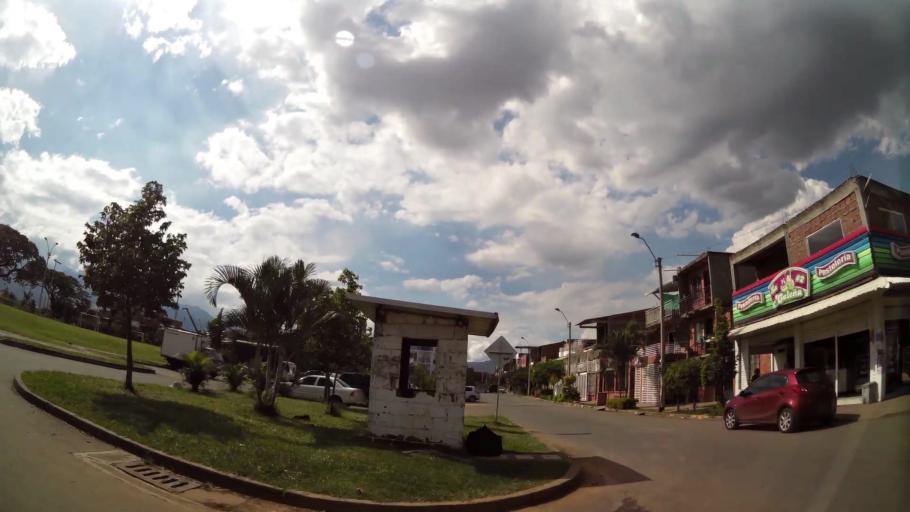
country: CO
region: Valle del Cauca
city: Cali
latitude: 3.3934
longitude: -76.5106
